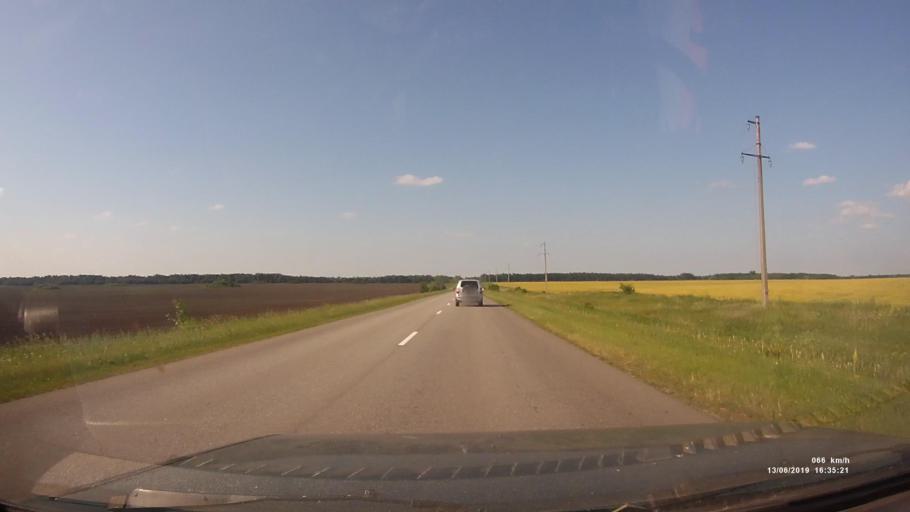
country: RU
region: Rostov
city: Kazanskaya
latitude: 49.8814
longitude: 41.2980
